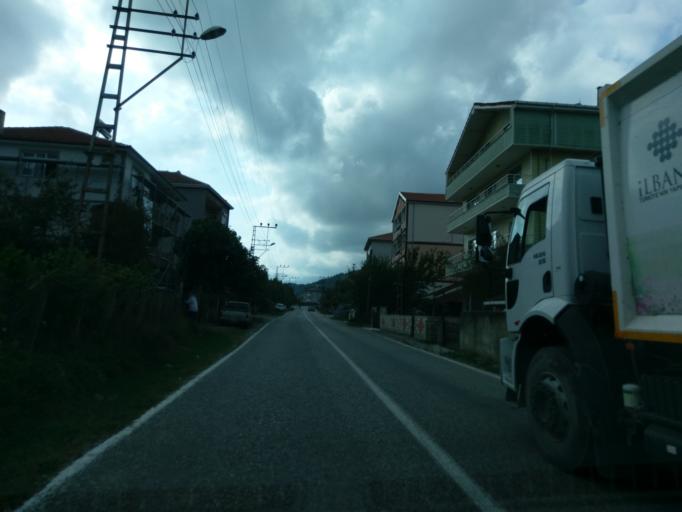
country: TR
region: Sinop
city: Helaldi
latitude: 41.9442
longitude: 34.3984
